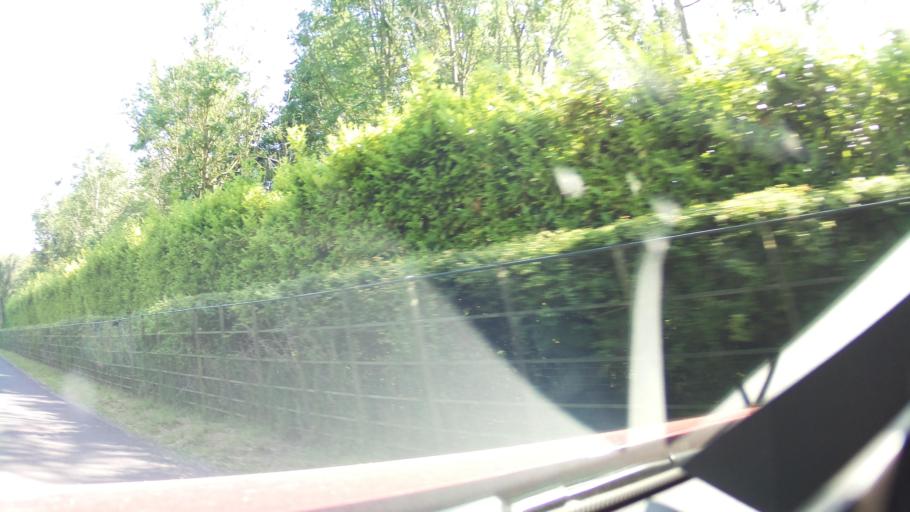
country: GB
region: England
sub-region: Hampshire
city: Overton
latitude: 51.2149
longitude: -1.3617
